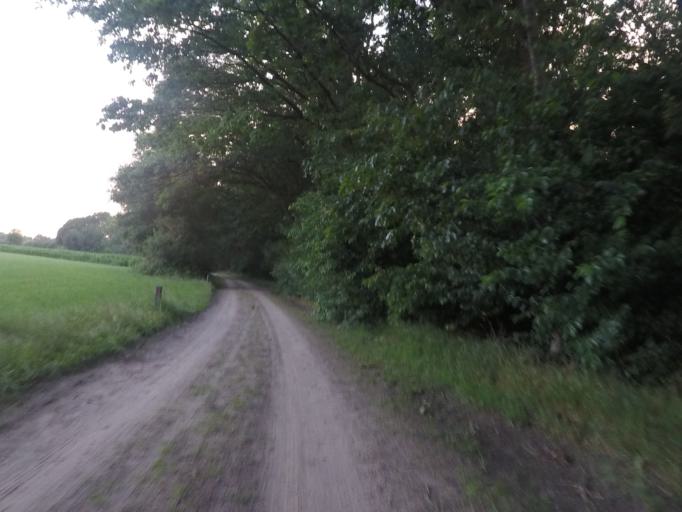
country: NL
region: Drenthe
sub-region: Gemeente Westerveld
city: Dwingeloo
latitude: 52.8630
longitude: 6.3175
